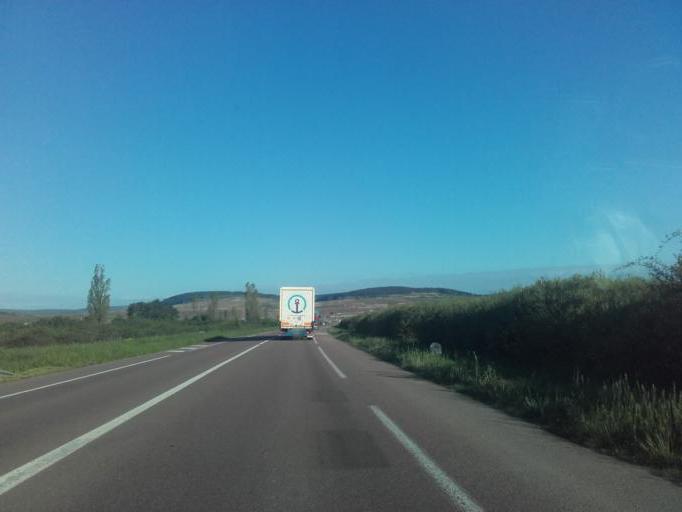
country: FR
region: Bourgogne
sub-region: Departement de la Cote-d'Or
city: Bligny-les-Beaune
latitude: 47.0069
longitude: 4.8238
